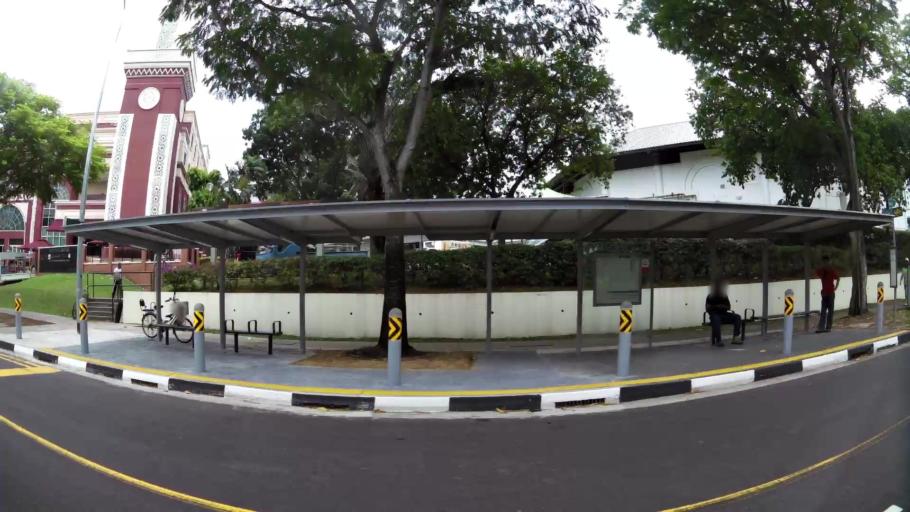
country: MY
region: Johor
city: Johor Bahru
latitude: 1.3348
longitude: 103.7196
